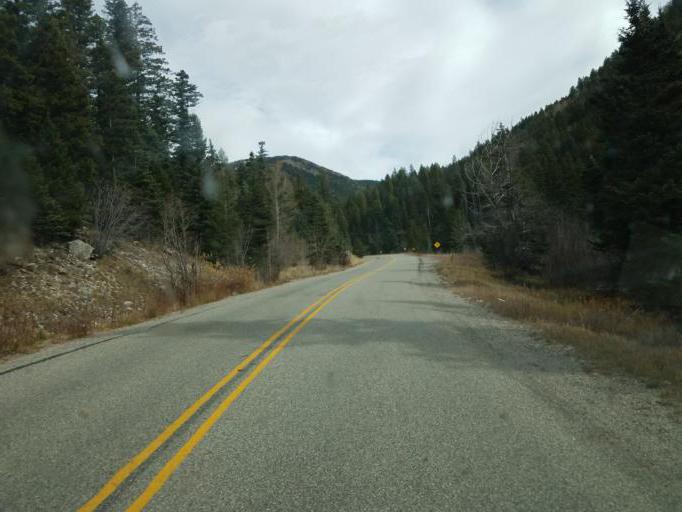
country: US
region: New Mexico
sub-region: Taos County
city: Arroyo Seco
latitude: 36.5899
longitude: -105.4891
